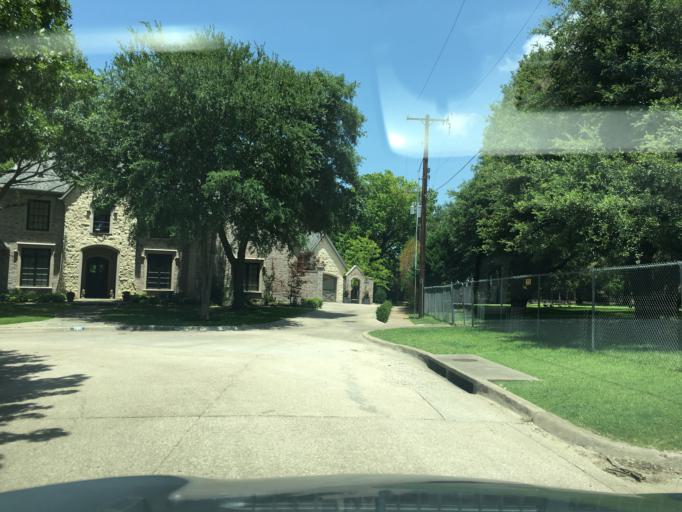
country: US
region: Texas
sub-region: Dallas County
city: University Park
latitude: 32.8816
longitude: -96.8066
